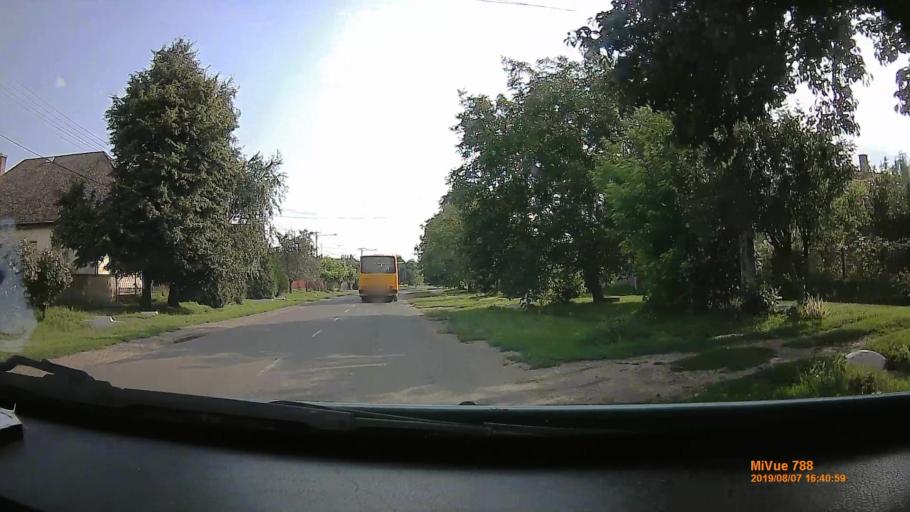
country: HU
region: Borsod-Abauj-Zemplen
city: Encs
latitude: 48.3815
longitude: 21.2154
